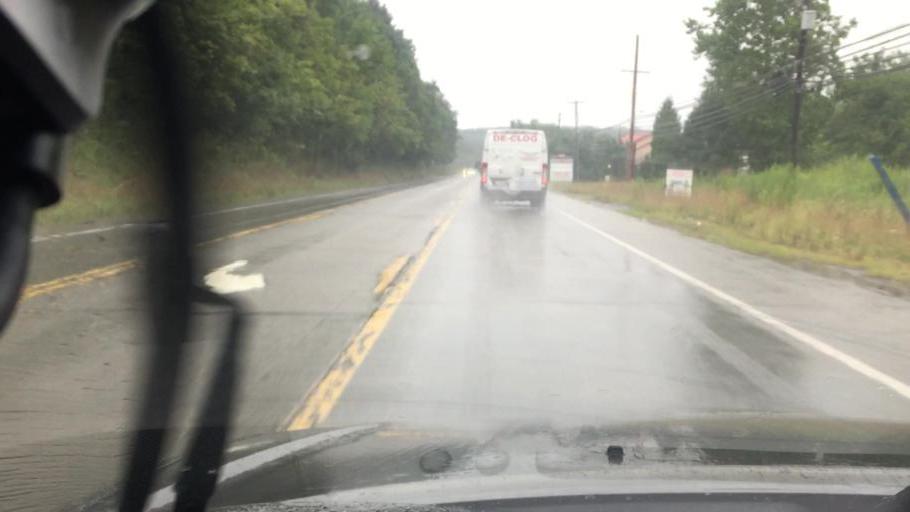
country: US
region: Pennsylvania
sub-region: Monroe County
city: Tannersville
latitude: 41.0209
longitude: -75.2972
